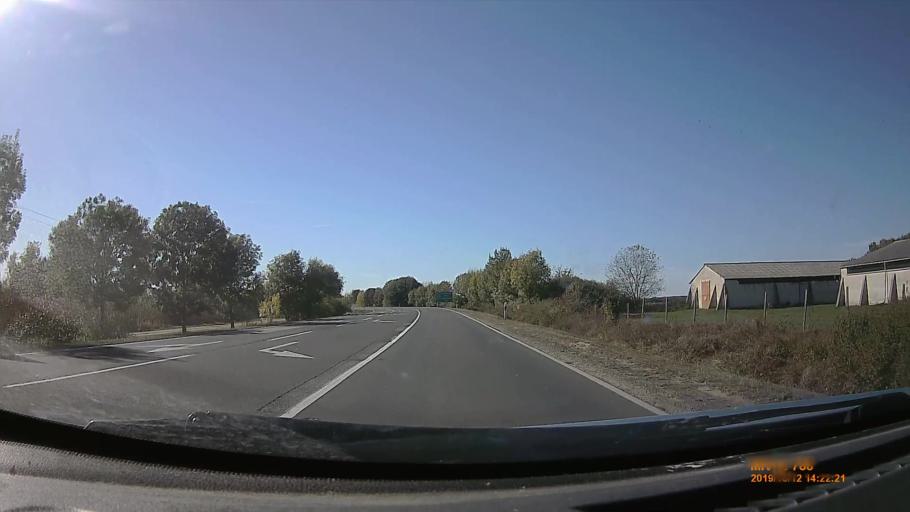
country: HU
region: Hajdu-Bihar
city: Biharkeresztes
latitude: 47.1423
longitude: 21.7170
